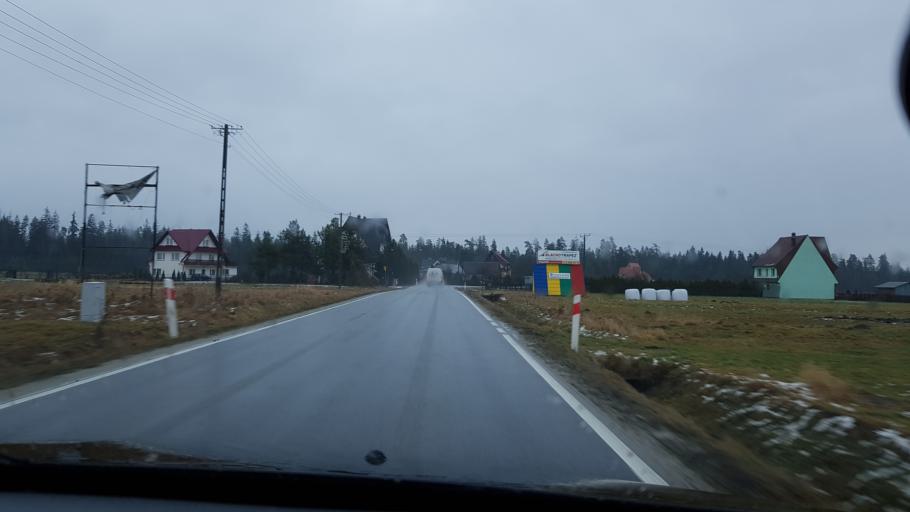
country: PL
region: Lesser Poland Voivodeship
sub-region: Powiat nowotarski
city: Lasek
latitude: 49.4890
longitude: 19.9717
